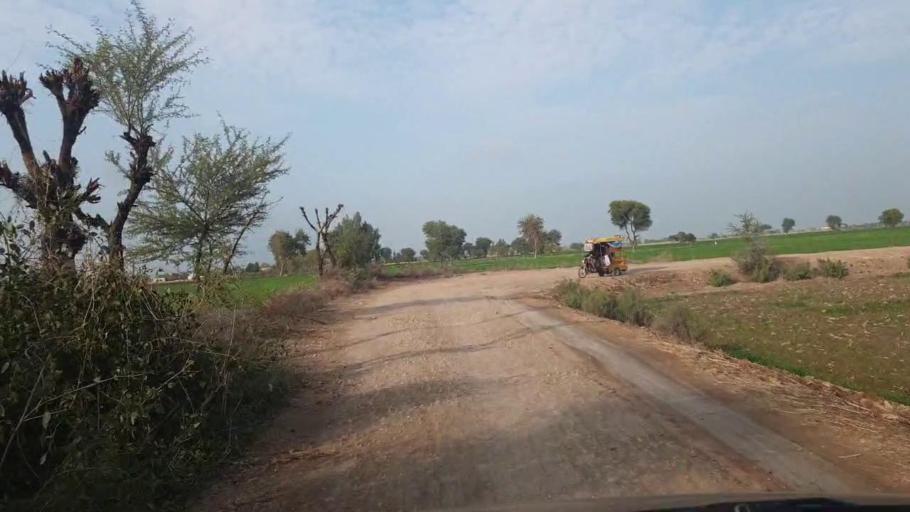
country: PK
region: Sindh
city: Shahdadpur
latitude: 25.8706
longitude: 68.7027
